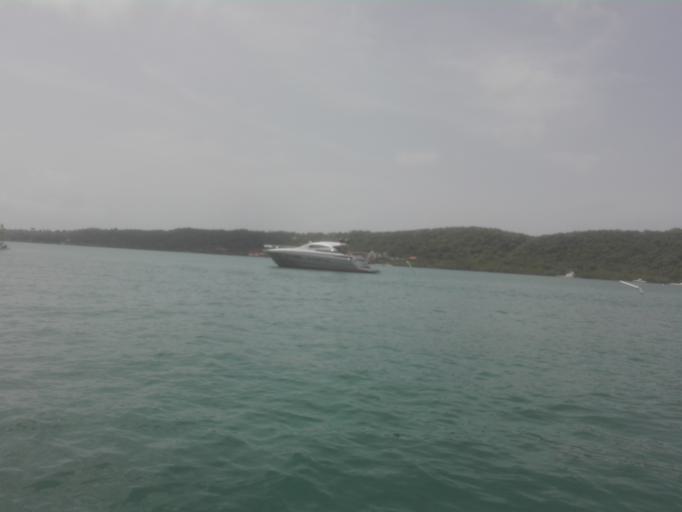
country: CO
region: Bolivar
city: Turbana
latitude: 10.1634
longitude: -75.6685
